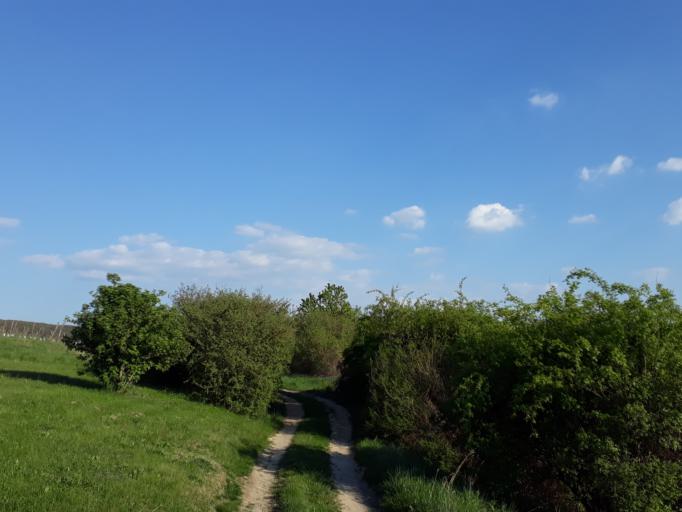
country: HU
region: Veszprem
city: Zanka
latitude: 46.9143
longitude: 17.6834
